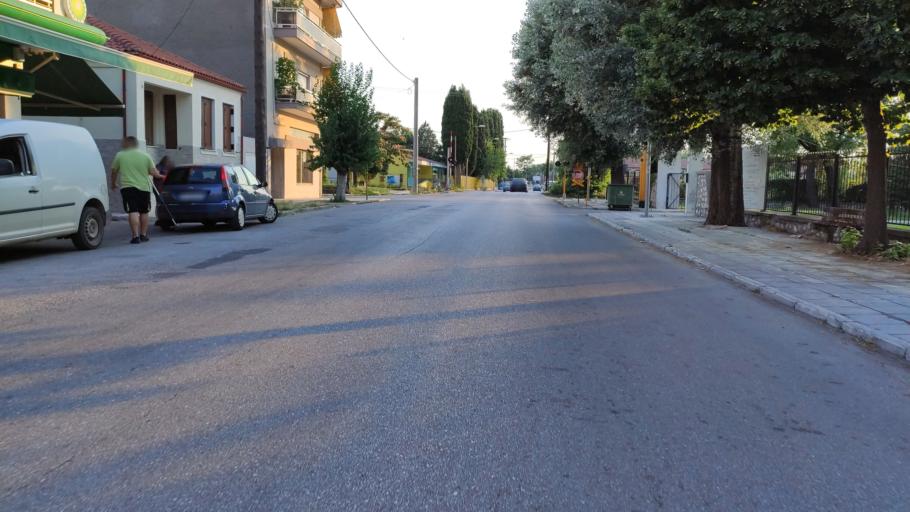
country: GR
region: East Macedonia and Thrace
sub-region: Nomos Rodopis
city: Komotini
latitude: 41.1174
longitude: 25.3899
